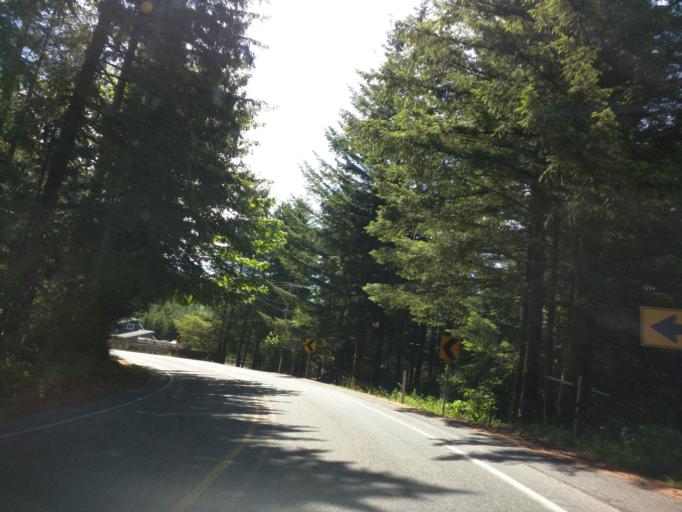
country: US
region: Washington
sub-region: Whatcom County
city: Peaceful Valley
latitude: 48.9357
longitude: -122.1460
